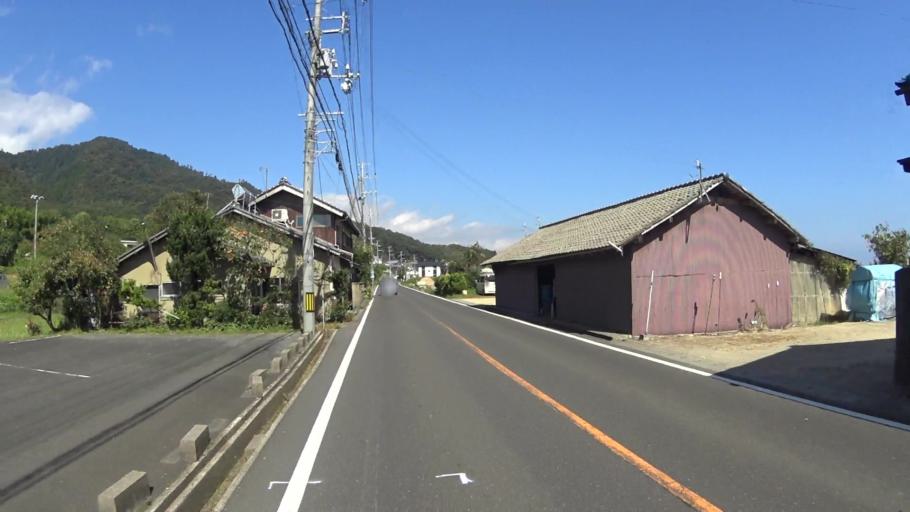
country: JP
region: Kyoto
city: Miyazu
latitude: 35.5902
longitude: 135.1941
